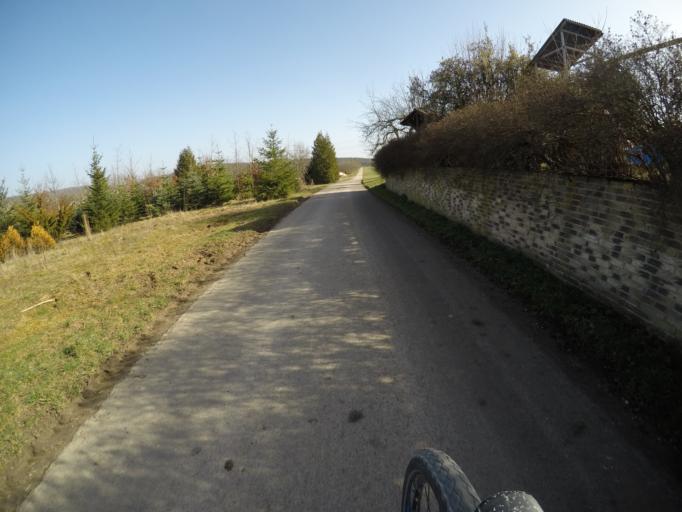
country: DE
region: Baden-Wuerttemberg
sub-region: Regierungsbezirk Stuttgart
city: Hochdorf
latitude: 48.6881
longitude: 9.4657
